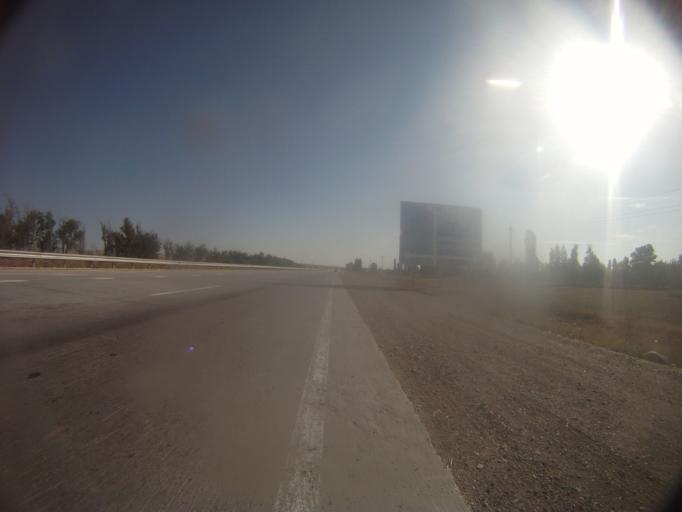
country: KZ
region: Ongtustik Qazaqstan
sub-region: Tulkibas Audany
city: Zhabagly
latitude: 42.6641
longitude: 70.8003
